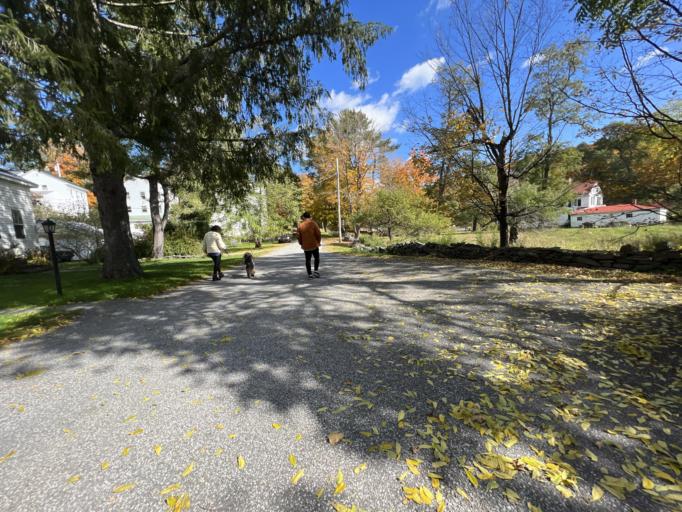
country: US
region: New York
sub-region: Albany County
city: Altamont
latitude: 42.5148
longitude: -74.1354
